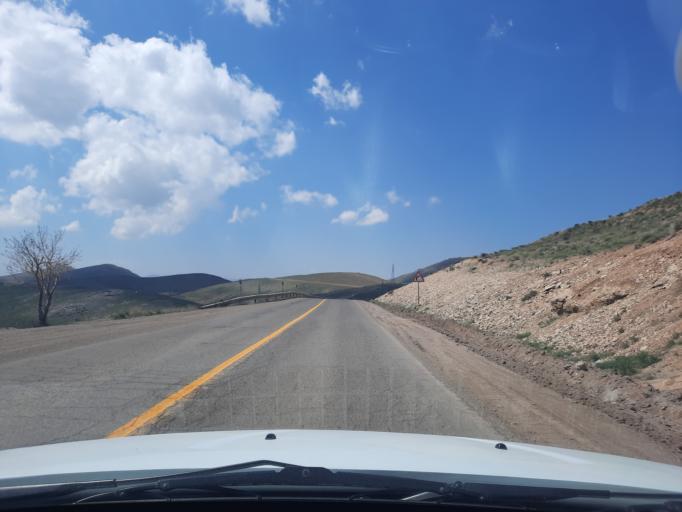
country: IR
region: Qazvin
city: Qazvin
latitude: 36.3894
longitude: 50.2094
